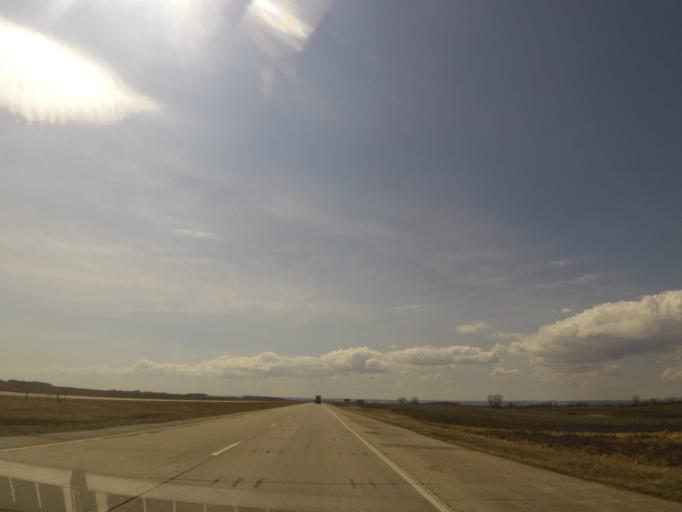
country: US
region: South Dakota
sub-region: Roberts County
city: Sisseton
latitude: 45.7328
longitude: -96.9403
